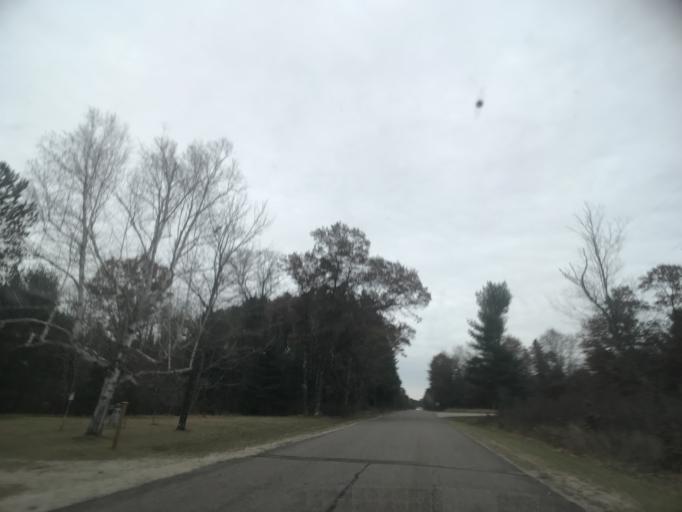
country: US
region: Wisconsin
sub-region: Oconto County
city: Gillett
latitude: 45.2813
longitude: -88.2570
